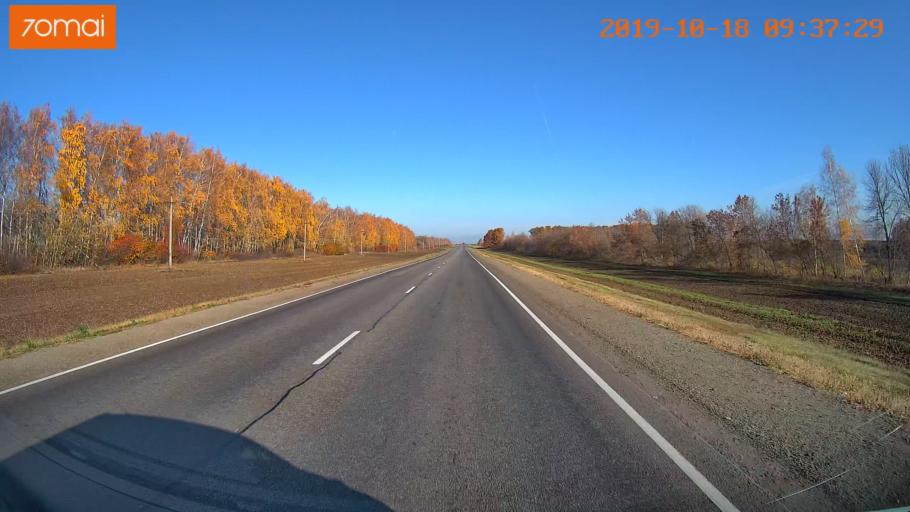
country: RU
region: Tula
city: Yefremov
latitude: 53.2230
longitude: 38.1409
